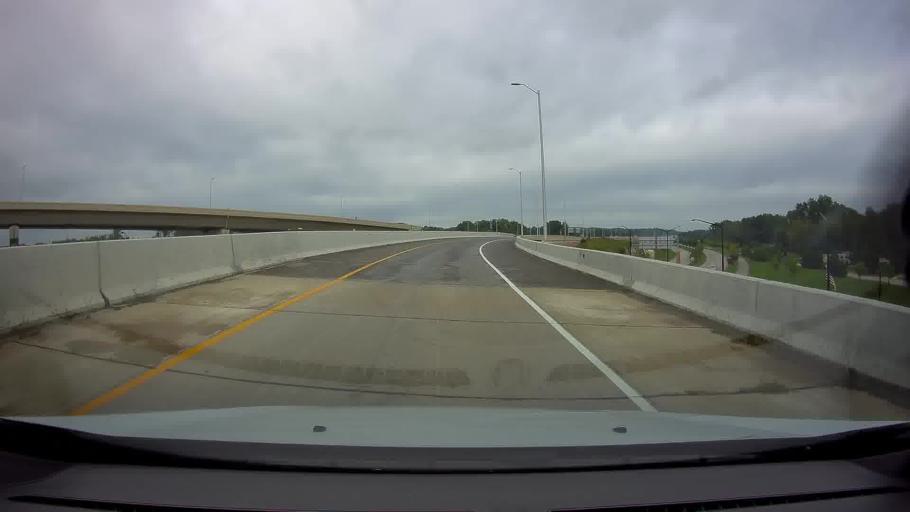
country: US
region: Wisconsin
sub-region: Brown County
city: Howard
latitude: 44.5404
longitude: -88.0792
